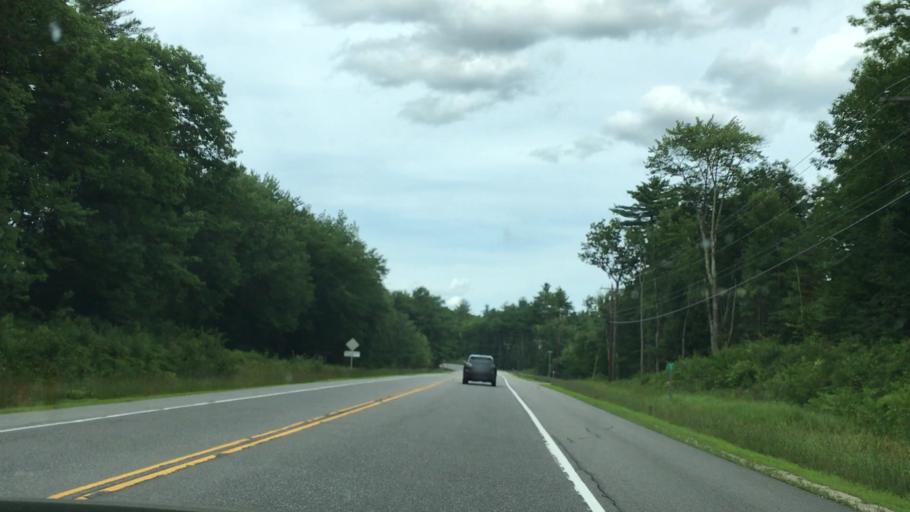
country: US
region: New Hampshire
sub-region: Belknap County
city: Meredith
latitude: 43.6278
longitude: -71.5355
